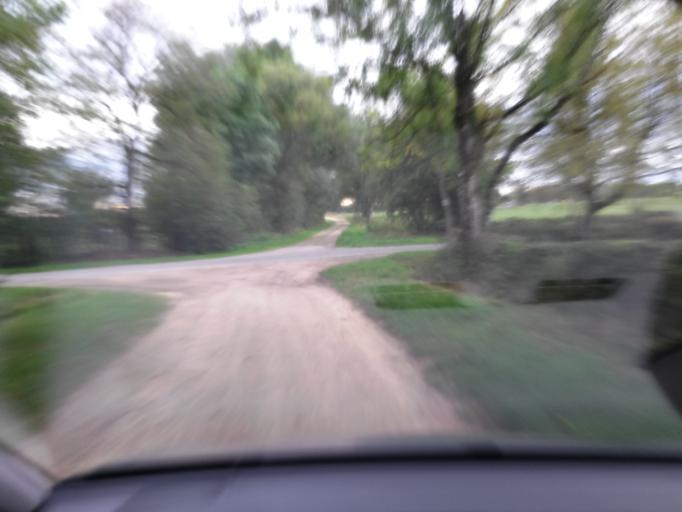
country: BE
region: Wallonia
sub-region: Province du Luxembourg
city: Habay-la-Vieille
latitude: 49.6806
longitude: 5.6580
